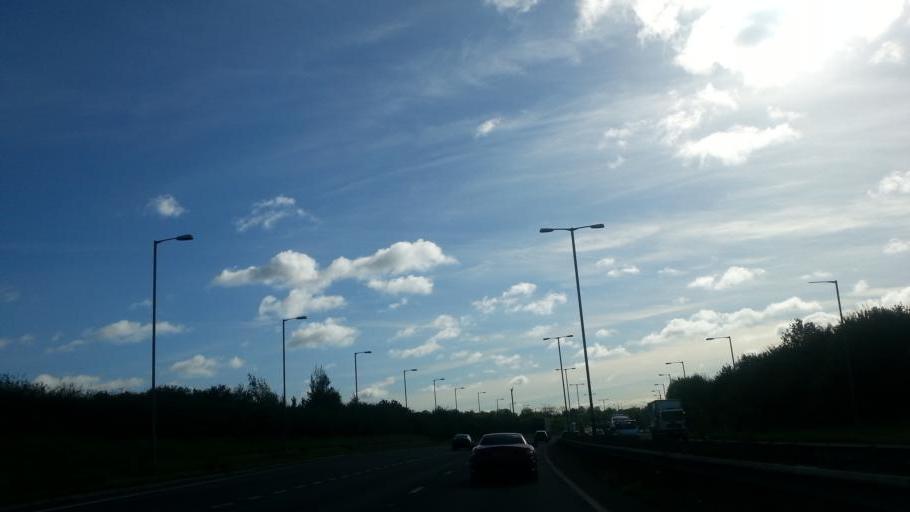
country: GB
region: England
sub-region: Northamptonshire
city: Kettering
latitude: 52.4112
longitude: -0.7599
